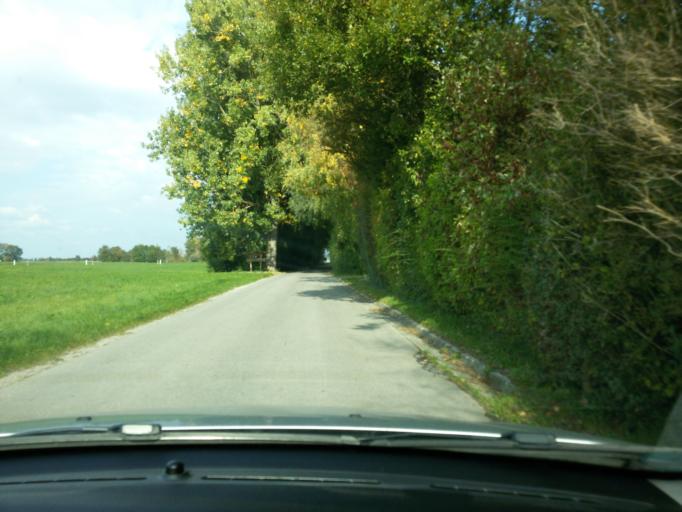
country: DE
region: Bavaria
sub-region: Swabia
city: Lamerdingen
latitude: 48.0836
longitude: 10.7817
